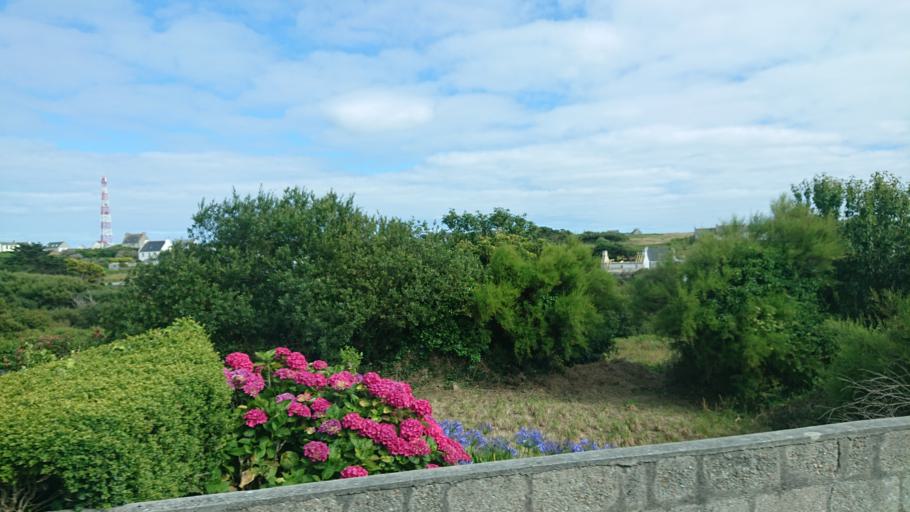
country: FR
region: Brittany
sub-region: Departement du Finistere
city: Porspoder
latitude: 48.4582
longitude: -5.0942
